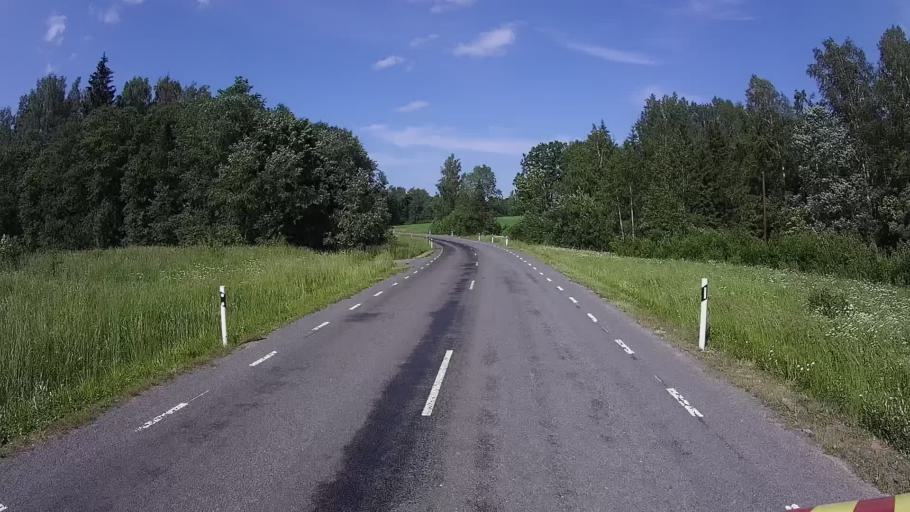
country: EE
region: Viljandimaa
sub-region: Karksi vald
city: Karksi-Nuia
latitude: 58.0868
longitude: 25.5580
